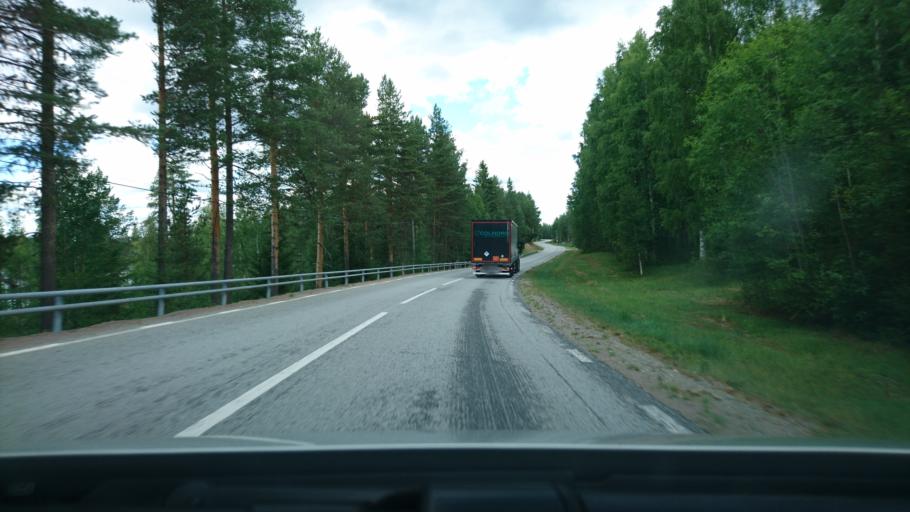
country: SE
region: Vaesterbotten
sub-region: Asele Kommun
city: Asele
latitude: 63.8314
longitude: 17.1573
